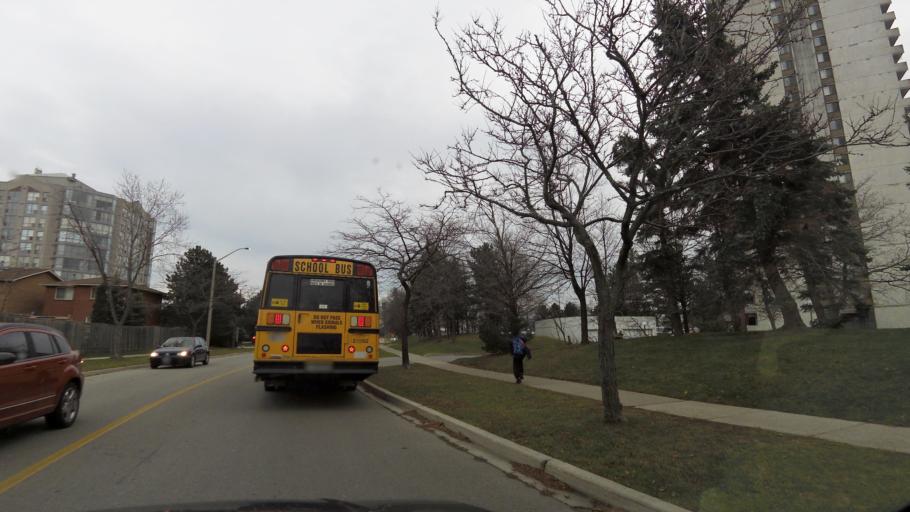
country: CA
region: Ontario
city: Etobicoke
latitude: 43.6285
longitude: -79.6074
